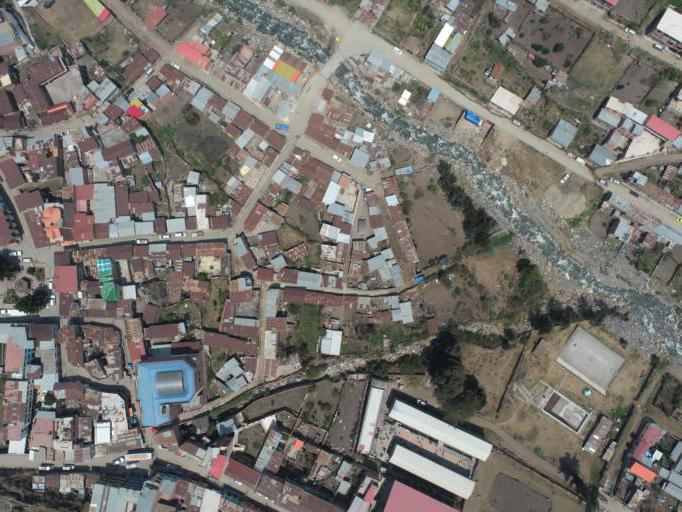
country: BO
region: La Paz
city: Quime
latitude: -16.9788
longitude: -67.2153
